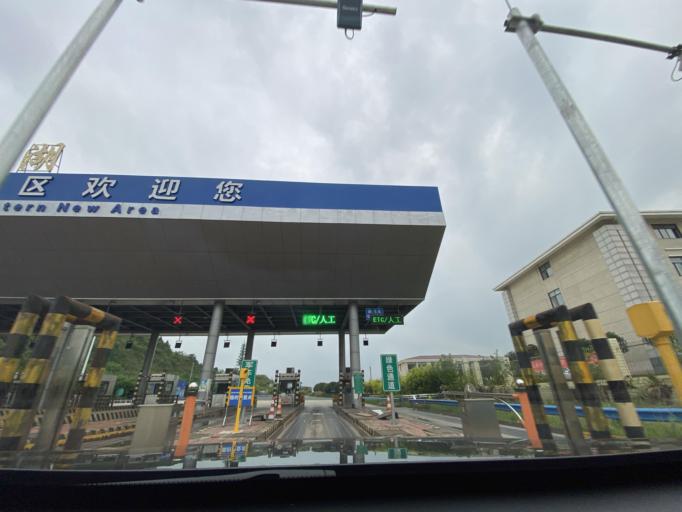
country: CN
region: Sichuan
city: Jiancheng
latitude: 30.4994
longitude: 104.4472
